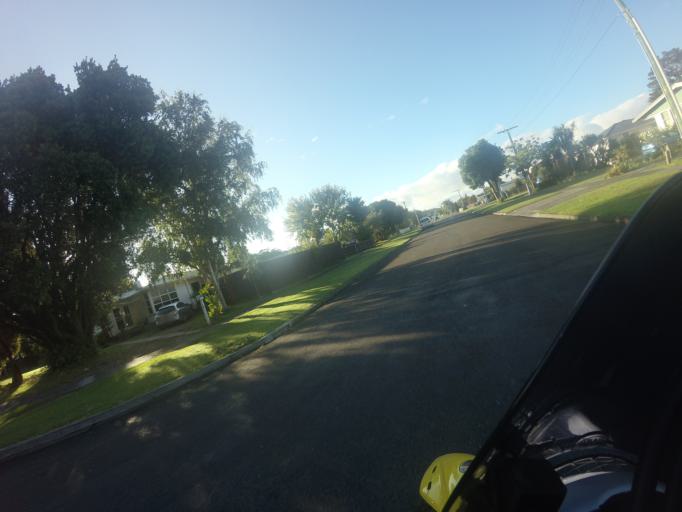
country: NZ
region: Gisborne
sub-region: Gisborne District
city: Gisborne
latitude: -38.6665
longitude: 178.0457
